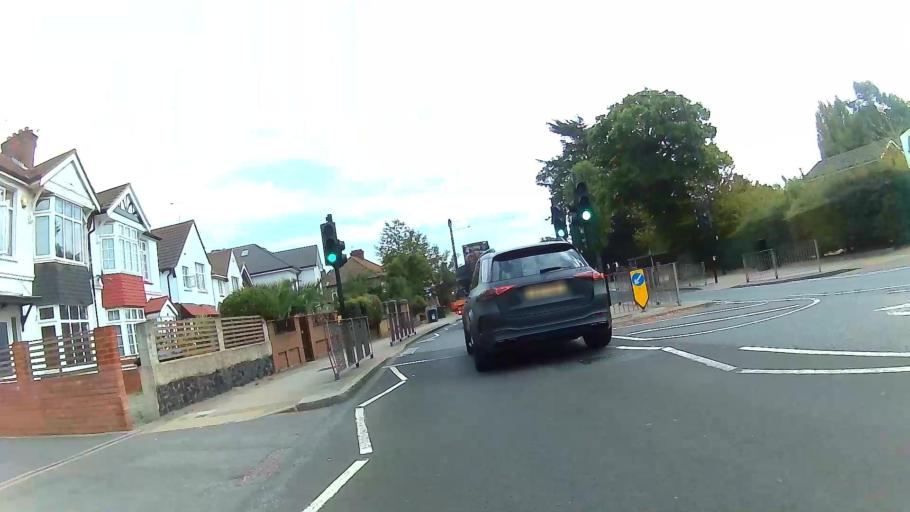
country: GB
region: England
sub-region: Hertfordshire
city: Waltham Cross
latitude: 51.6811
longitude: -0.0414
